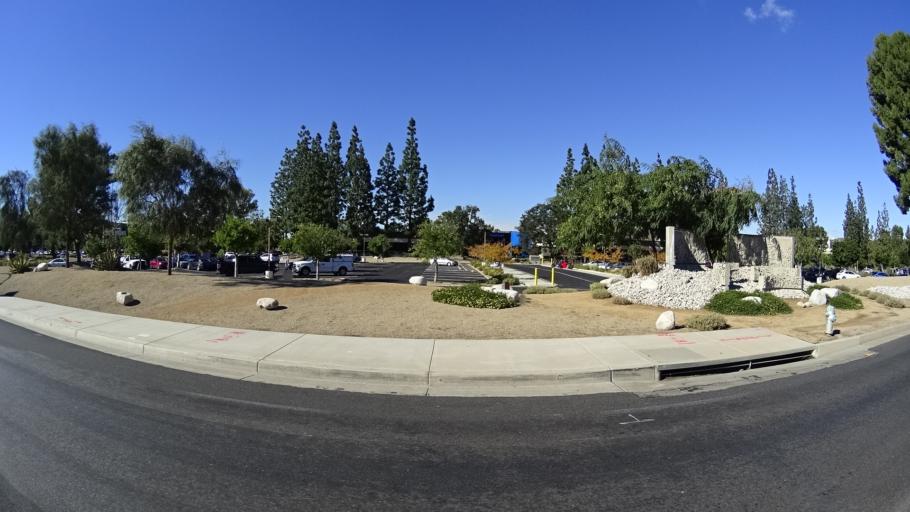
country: US
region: California
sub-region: Orange County
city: Placentia
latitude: 33.9106
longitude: -117.8518
